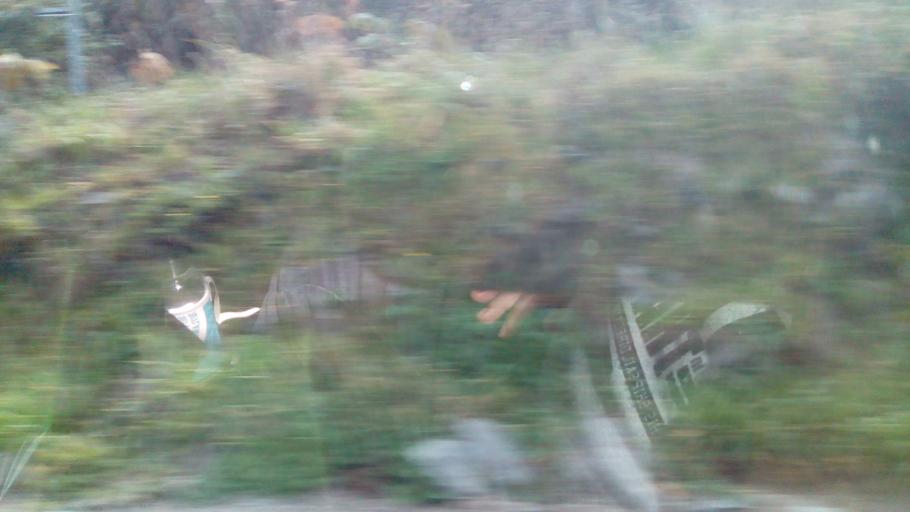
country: TW
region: Taiwan
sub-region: Hualien
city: Hualian
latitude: 24.3621
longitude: 121.3319
